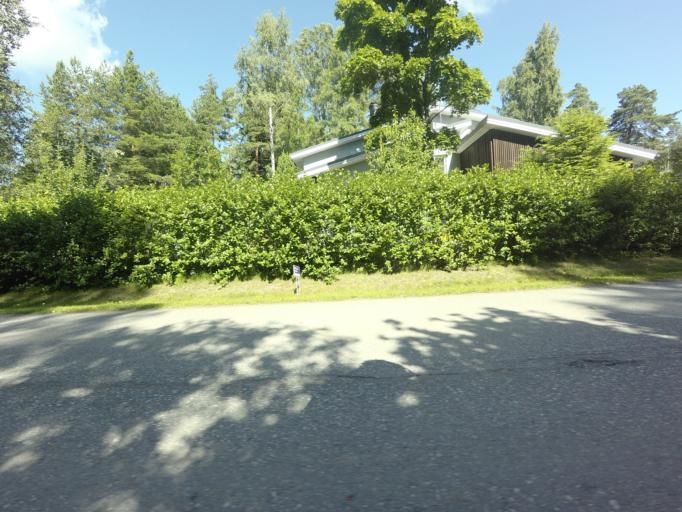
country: FI
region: Uusimaa
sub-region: Helsinki
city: Espoo
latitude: 60.1641
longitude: 24.6848
